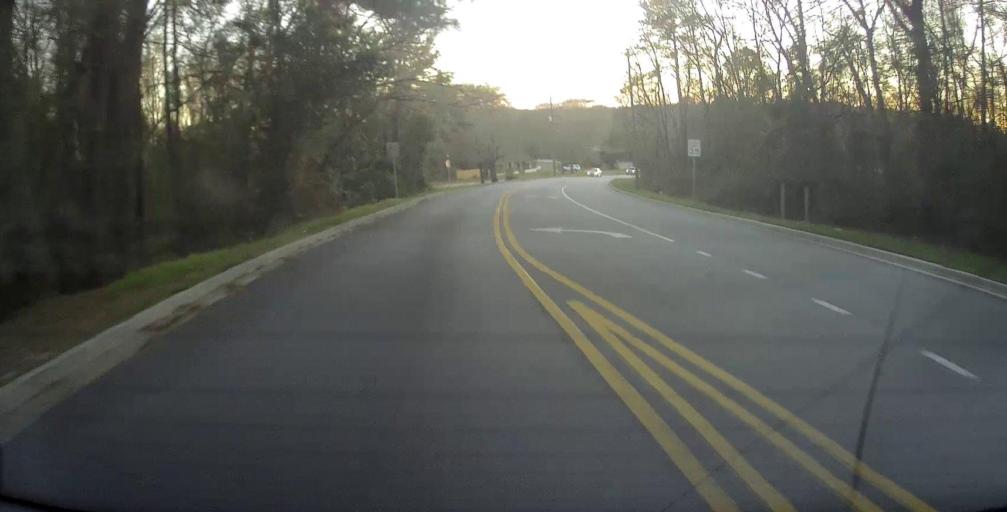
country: US
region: Alabama
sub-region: Russell County
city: Phenix City
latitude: 32.4865
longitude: -85.0210
